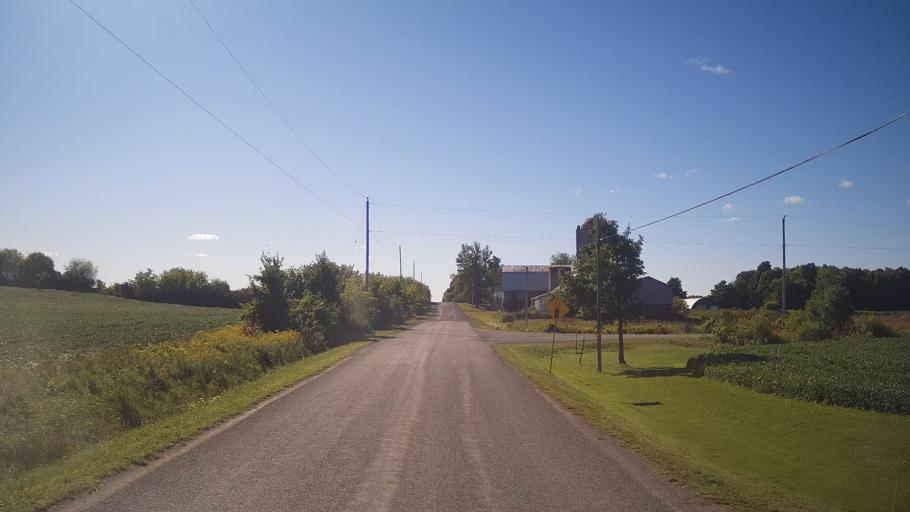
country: CA
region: Ontario
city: Prescott
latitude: 44.9778
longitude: -75.5743
